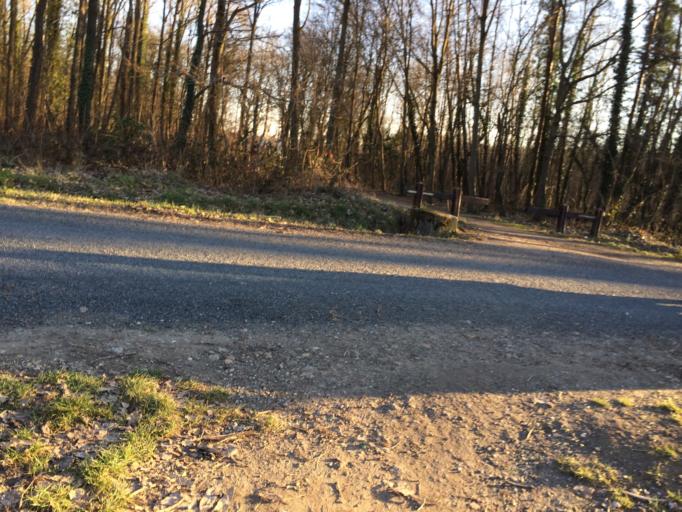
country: FR
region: Ile-de-France
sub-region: Departement de l'Essonne
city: Villebon-sur-Yvette
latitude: 48.7144
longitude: 2.2263
